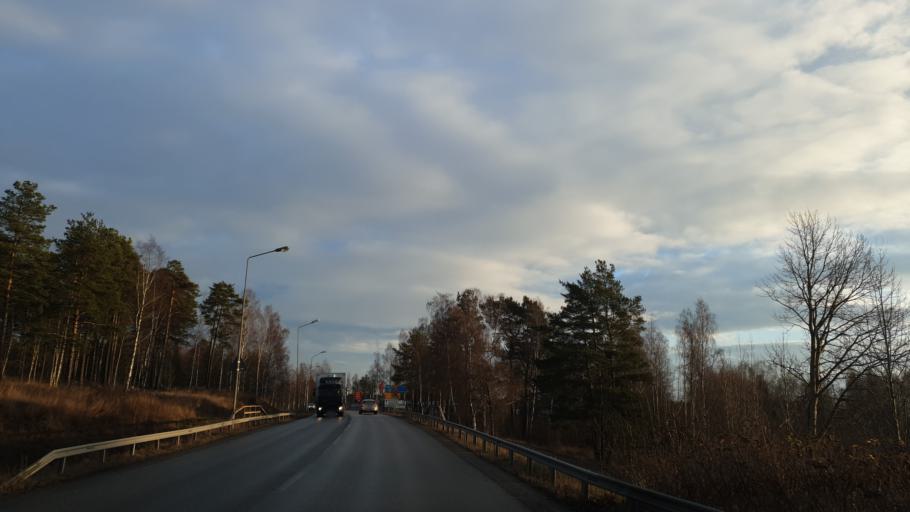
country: SE
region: Gaevleborg
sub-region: Hudiksvalls Kommun
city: Hudiksvall
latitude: 61.7242
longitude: 17.1409
